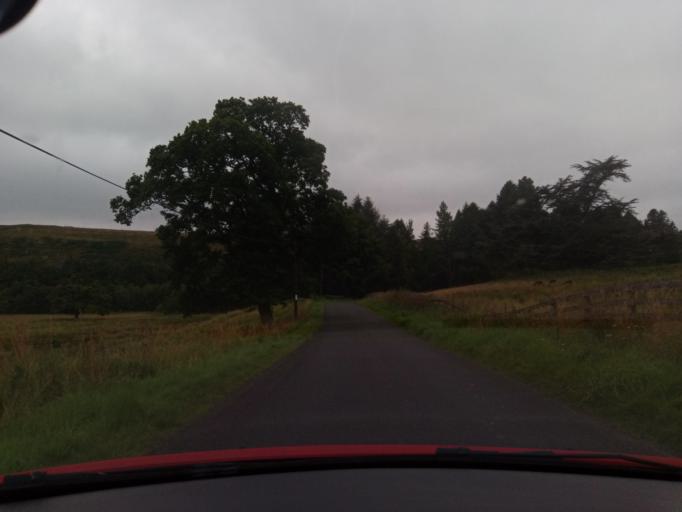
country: GB
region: England
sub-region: Northumberland
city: Otterburn
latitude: 55.2966
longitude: -2.0529
